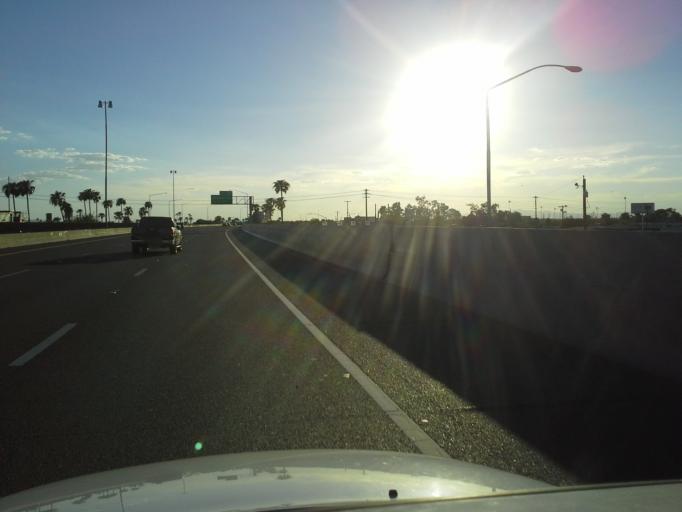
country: US
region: Arizona
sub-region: Maricopa County
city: Phoenix
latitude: 33.4292
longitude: -112.0973
